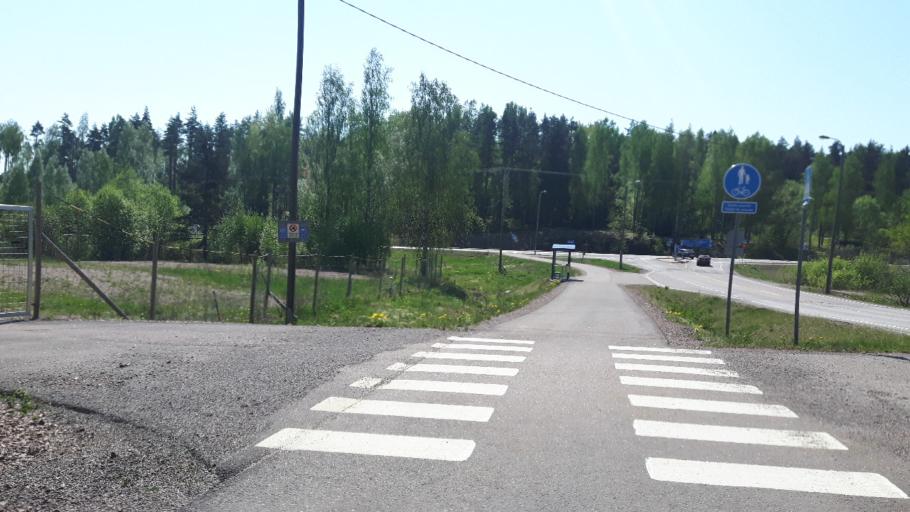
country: FI
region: Uusimaa
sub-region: Loviisa
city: Ruotsinpyhtaeae
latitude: 60.4964
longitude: 26.4419
